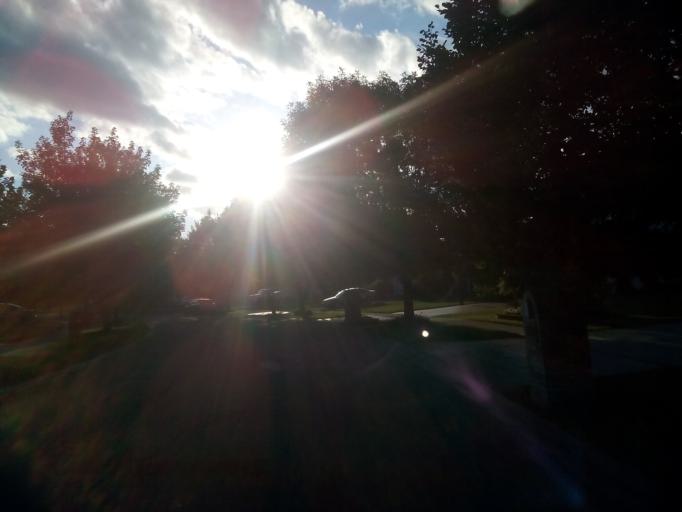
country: US
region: Illinois
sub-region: Will County
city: Romeoville
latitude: 41.6946
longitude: -88.1463
